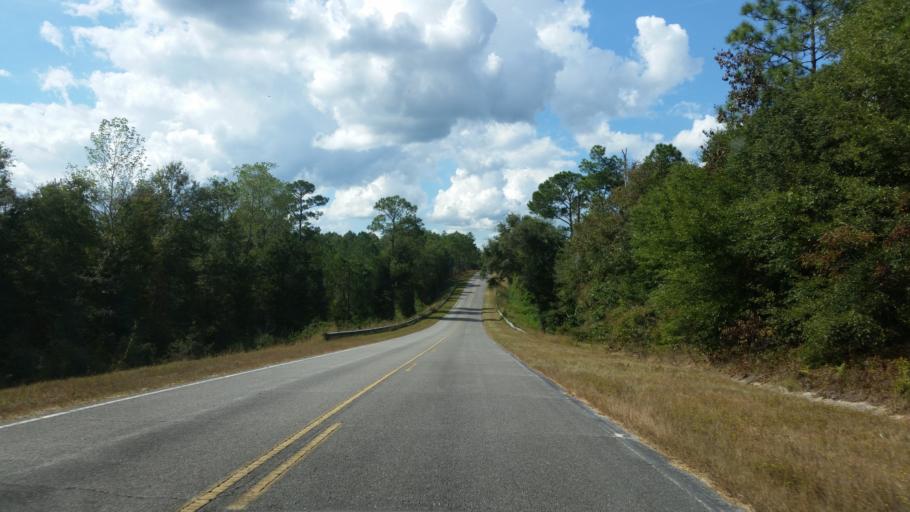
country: US
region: Alabama
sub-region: Escambia County
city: Atmore
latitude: 30.8856
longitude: -87.5202
